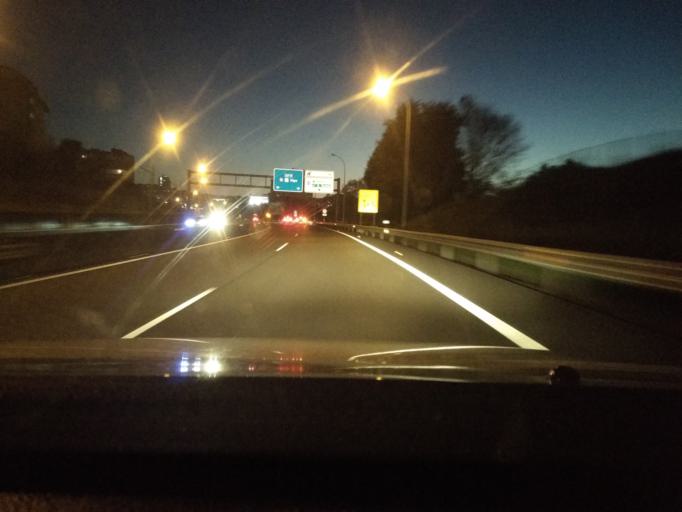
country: ES
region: Galicia
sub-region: Provincia de Pontevedra
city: Vigo
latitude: 42.2434
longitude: -8.7020
